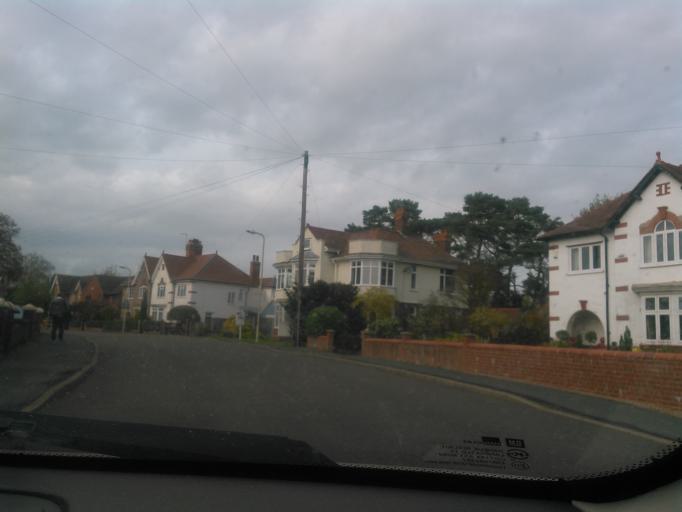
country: GB
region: England
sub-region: Shropshire
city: Wem
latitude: 52.8598
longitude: -2.7192
